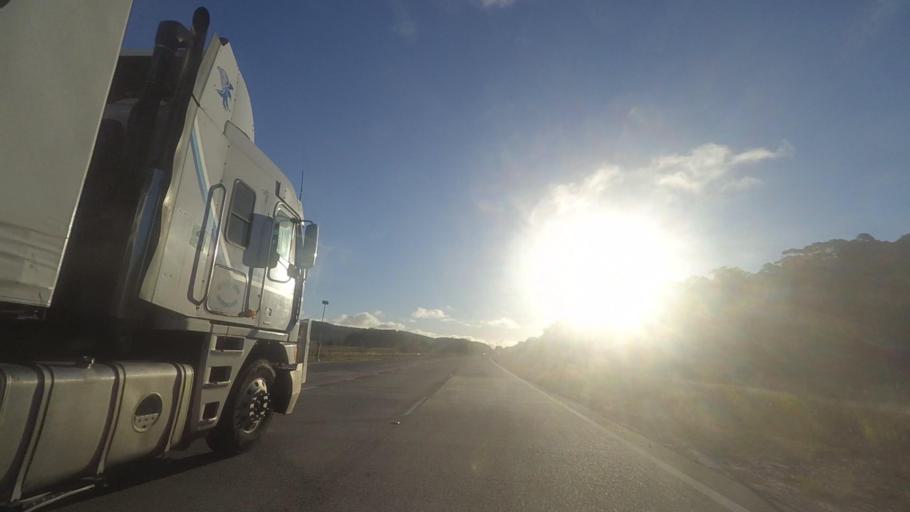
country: AU
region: New South Wales
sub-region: Great Lakes
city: Bulahdelah
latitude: -32.5217
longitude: 152.2023
